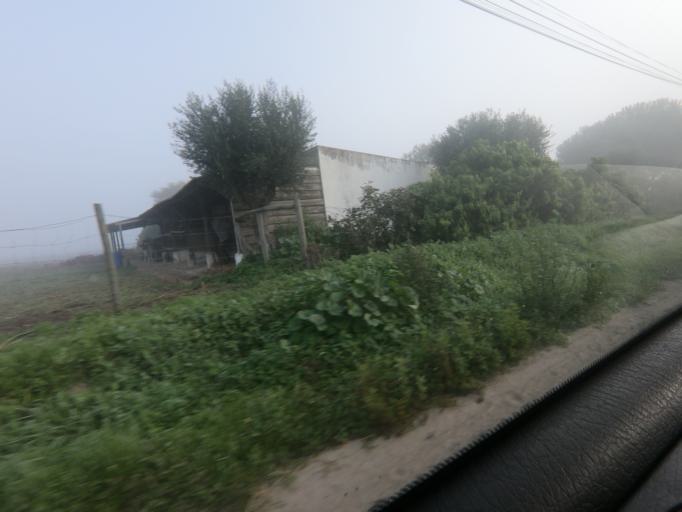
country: PT
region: Setubal
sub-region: Palmela
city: Pinhal Novo
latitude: 38.6120
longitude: -8.8762
